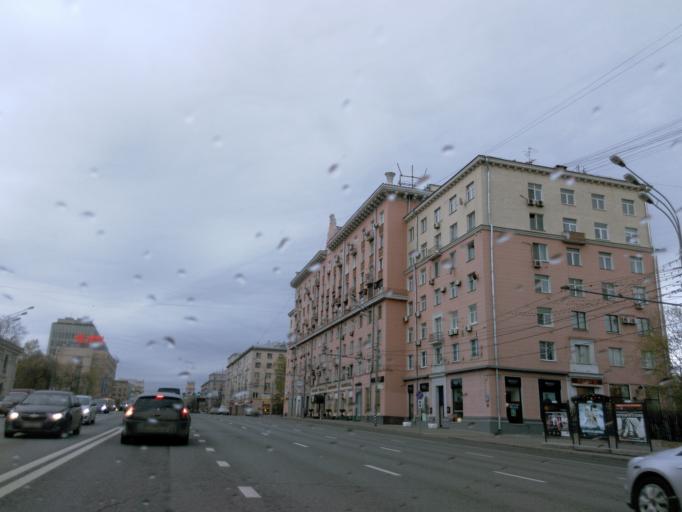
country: RU
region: Moscow
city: Novyye Cheremushki
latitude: 55.7163
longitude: 37.5930
